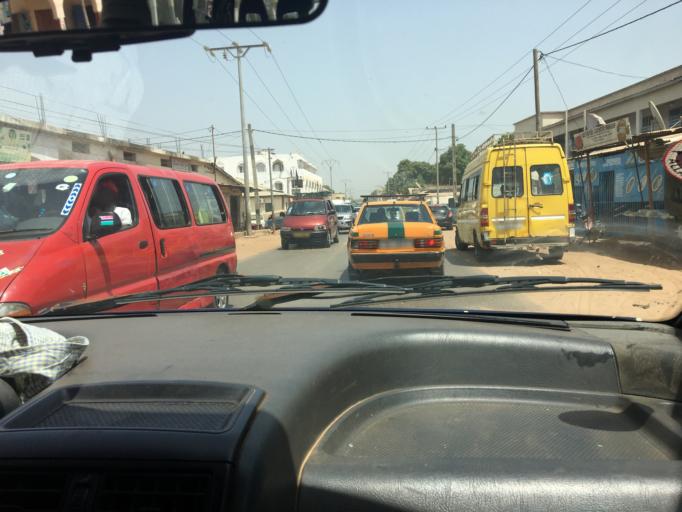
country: GM
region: Western
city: Abuko
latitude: 13.3977
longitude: -16.6733
